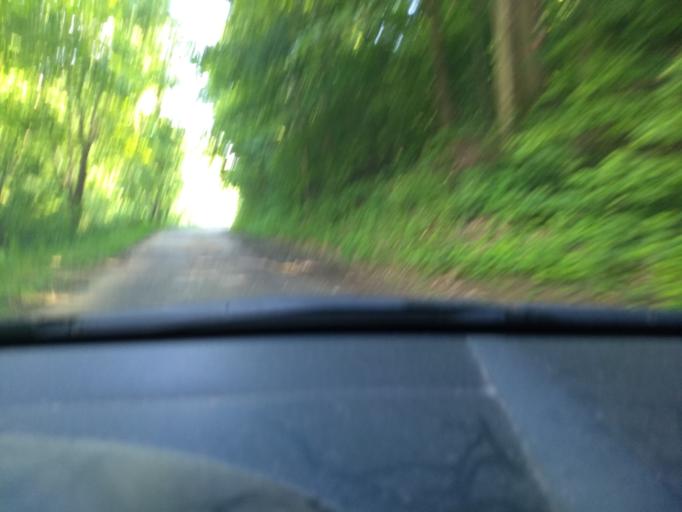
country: US
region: Indiana
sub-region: Floyd County
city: New Albany
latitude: 38.2741
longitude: -85.8676
